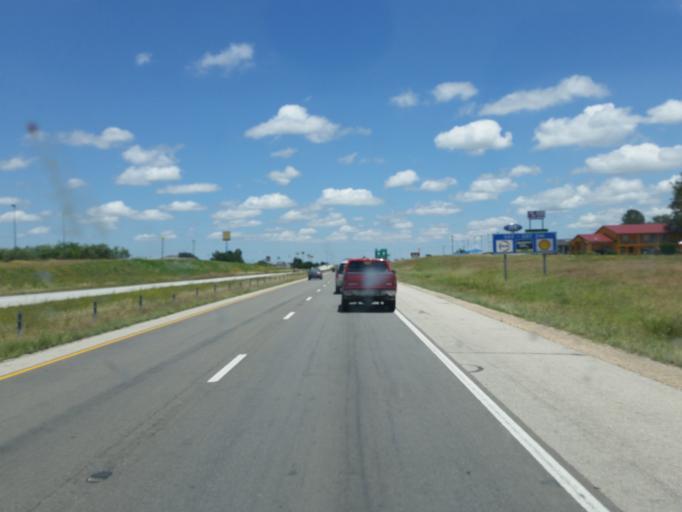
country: US
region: Texas
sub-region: Nolan County
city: Sweetwater
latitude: 32.4482
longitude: -100.4074
